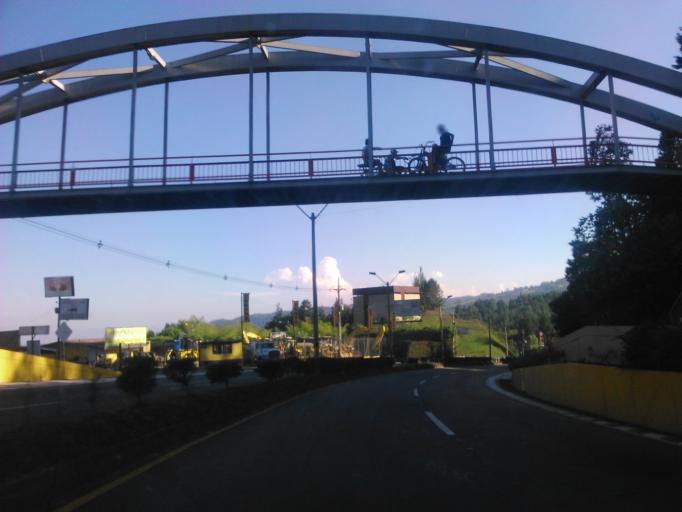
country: CO
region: Antioquia
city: Guarne
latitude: 6.3207
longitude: -75.4638
